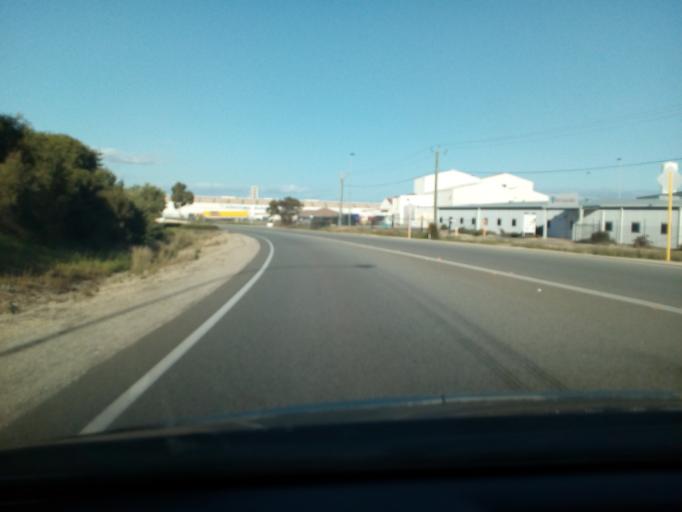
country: AU
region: Western Australia
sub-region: City of Cockburn
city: Coogee
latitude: -32.1484
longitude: 115.7720
